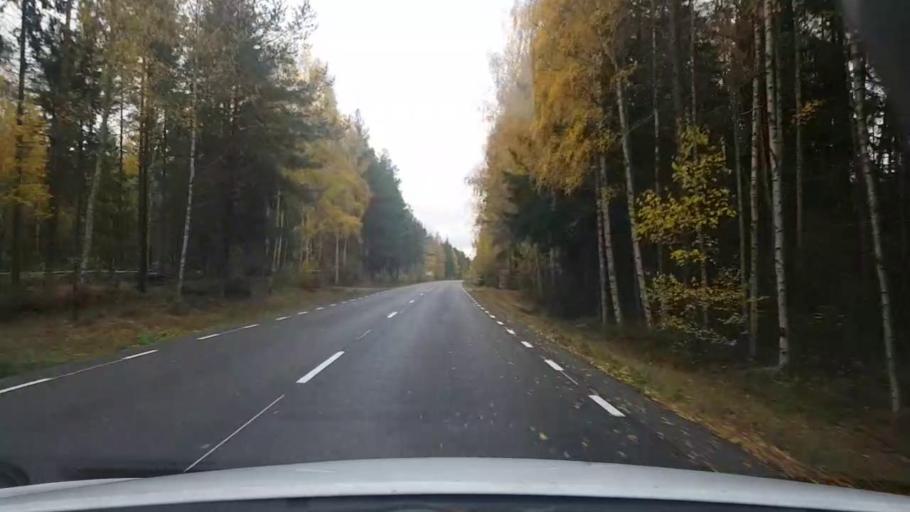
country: SE
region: OErebro
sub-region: Laxa Kommun
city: Laxa
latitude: 58.7971
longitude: 14.5422
